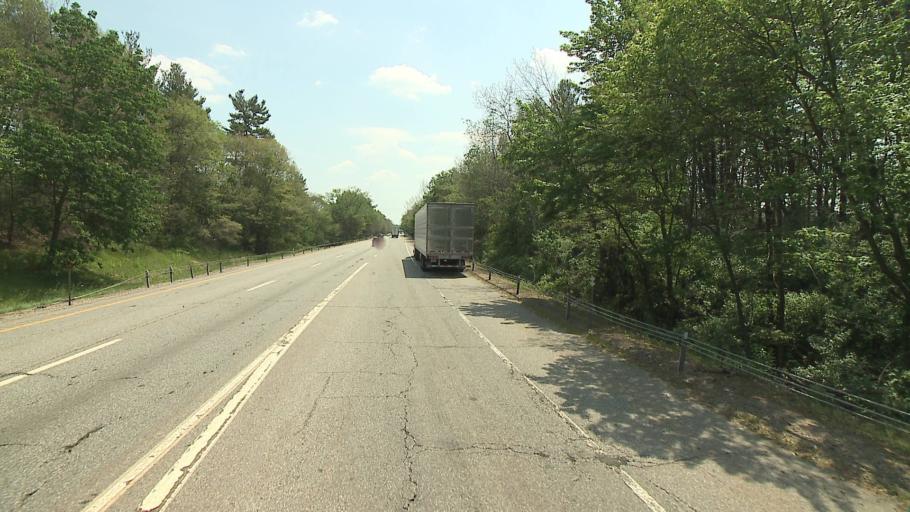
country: US
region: Connecticut
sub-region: Windham County
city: Killingly Center
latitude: 41.8644
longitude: -71.8881
